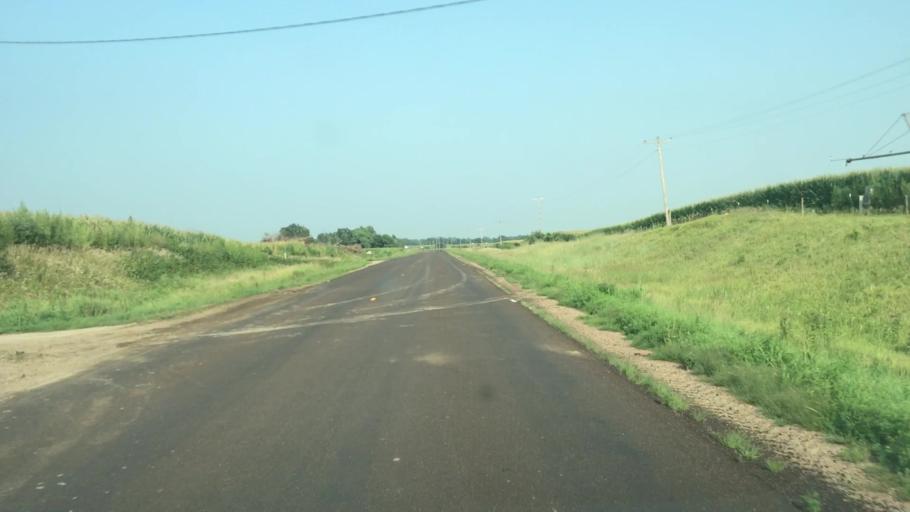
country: US
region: Nebraska
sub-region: Buffalo County
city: Ravenna
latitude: 41.0757
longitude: -98.7442
